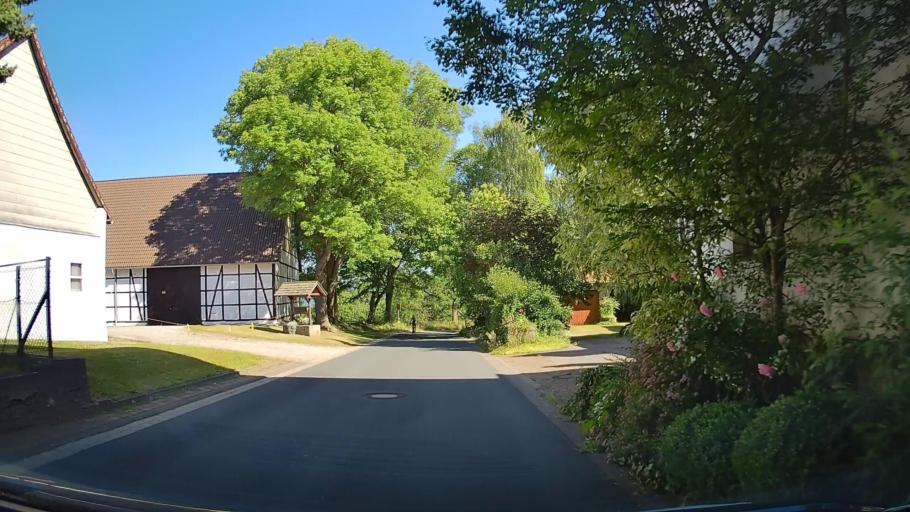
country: DE
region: Lower Saxony
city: Vahlbruch
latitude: 51.9700
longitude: 9.3544
